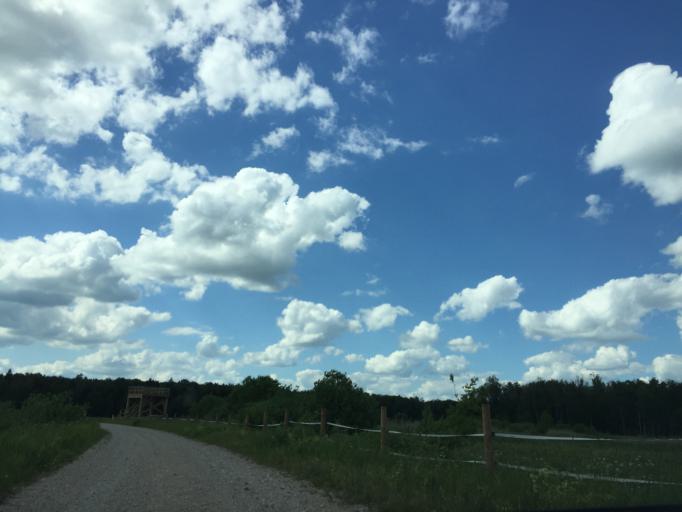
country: LV
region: Engure
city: Smarde
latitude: 56.8691
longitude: 23.3849
